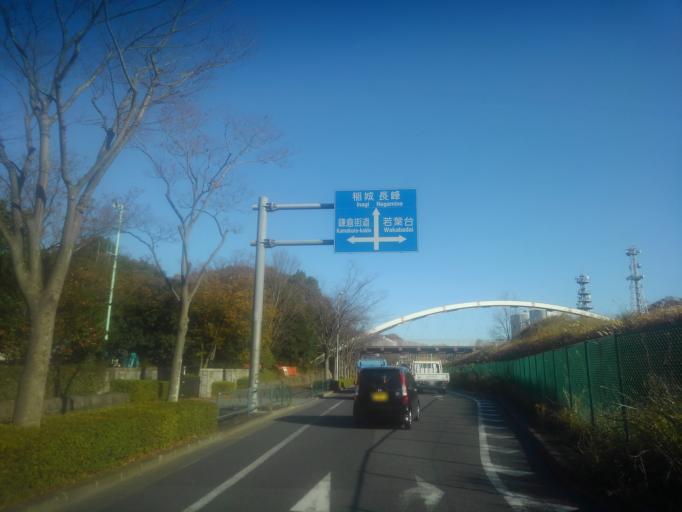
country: JP
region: Tokyo
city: Hino
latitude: 35.6248
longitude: 139.4614
